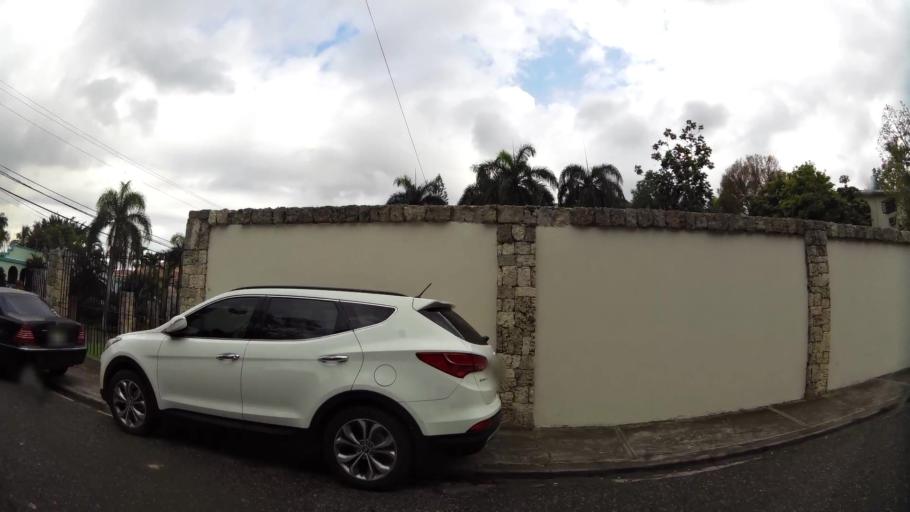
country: DO
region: Nacional
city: La Agustina
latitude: 18.4974
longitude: -69.9373
